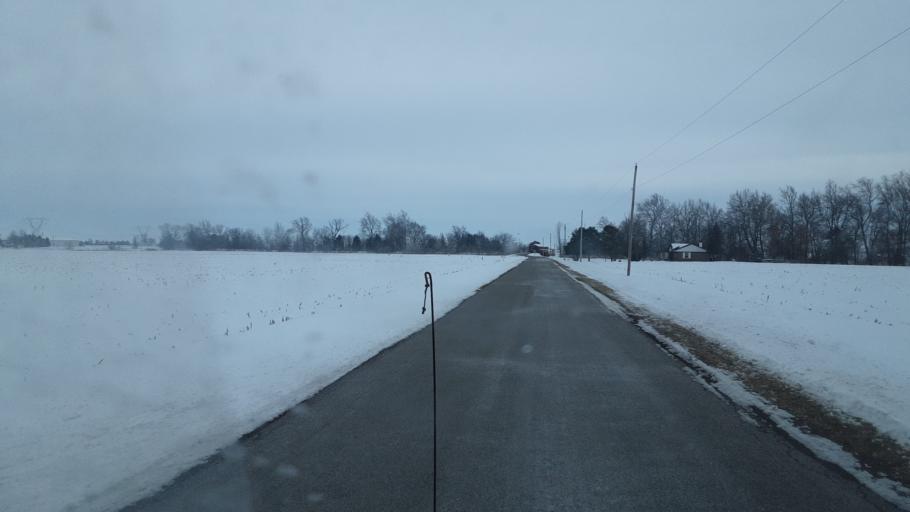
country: US
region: Ohio
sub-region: Union County
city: Marysville
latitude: 40.1201
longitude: -83.4243
